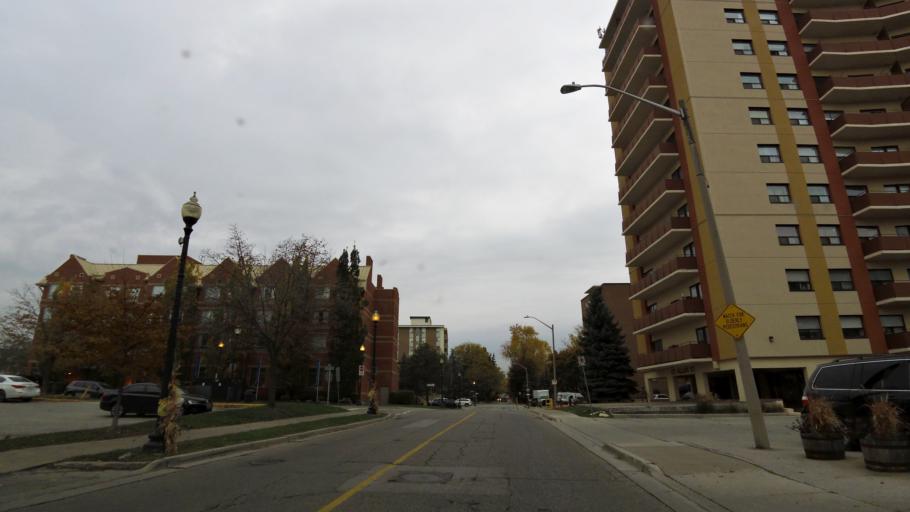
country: CA
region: Ontario
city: Oakville
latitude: 43.4493
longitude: -79.6651
